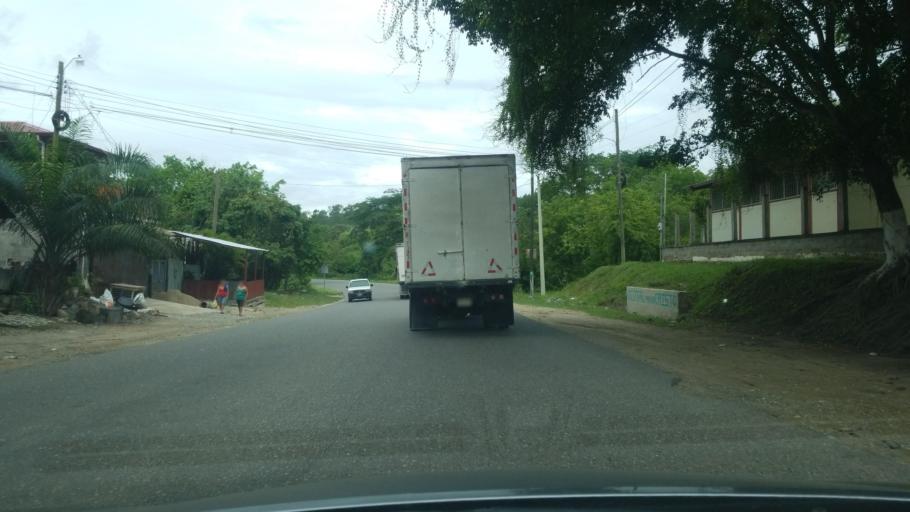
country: HN
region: Santa Barbara
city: San Marcos
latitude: 15.3135
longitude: -88.4370
